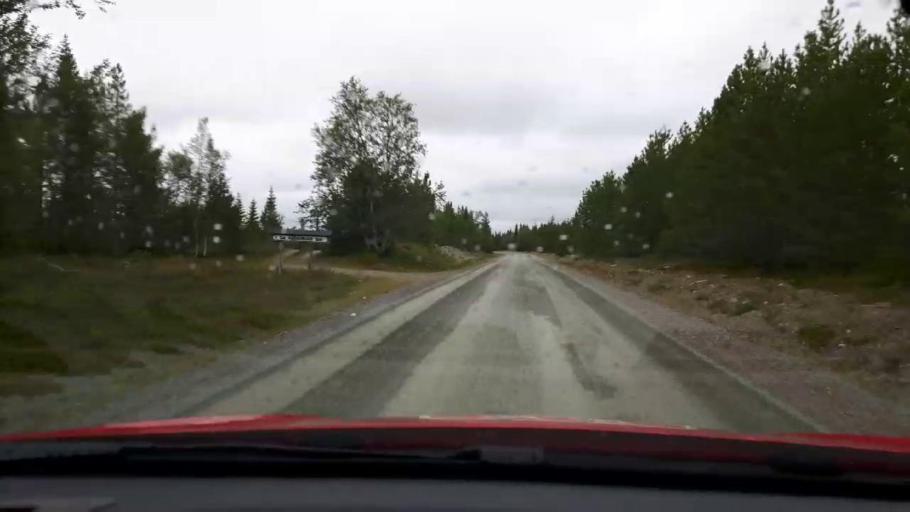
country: SE
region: Jaemtland
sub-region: Bergs Kommun
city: Hoverberg
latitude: 62.9020
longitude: 14.0614
